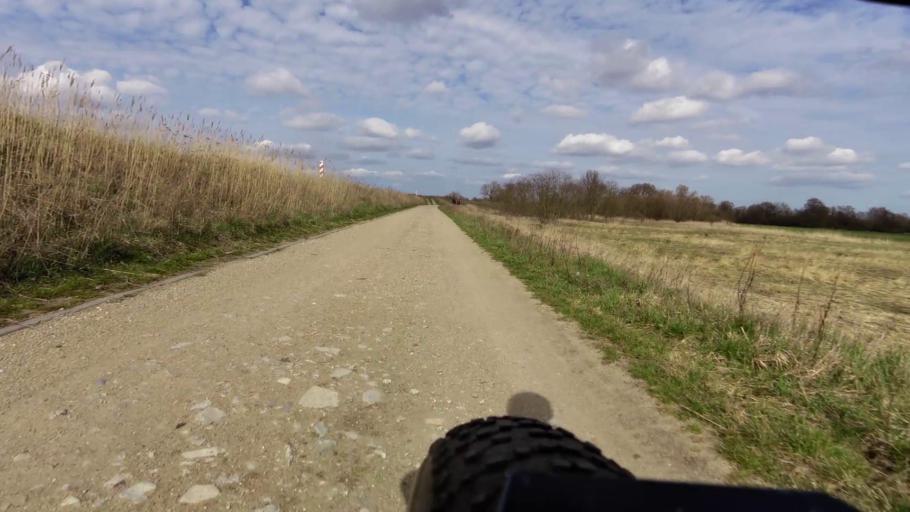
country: DE
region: Brandenburg
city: Lebus
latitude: 52.4267
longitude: 14.5482
